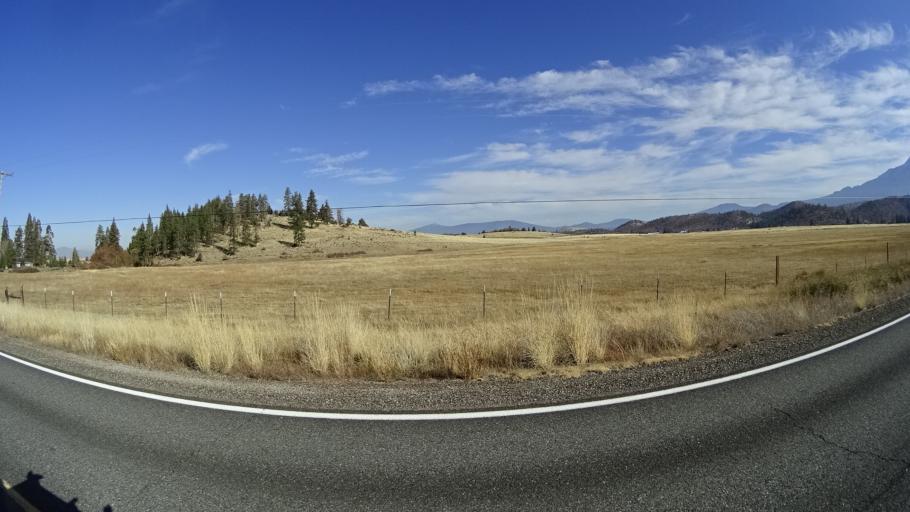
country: US
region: California
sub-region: Siskiyou County
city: Weed
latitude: 41.4468
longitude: -122.4477
